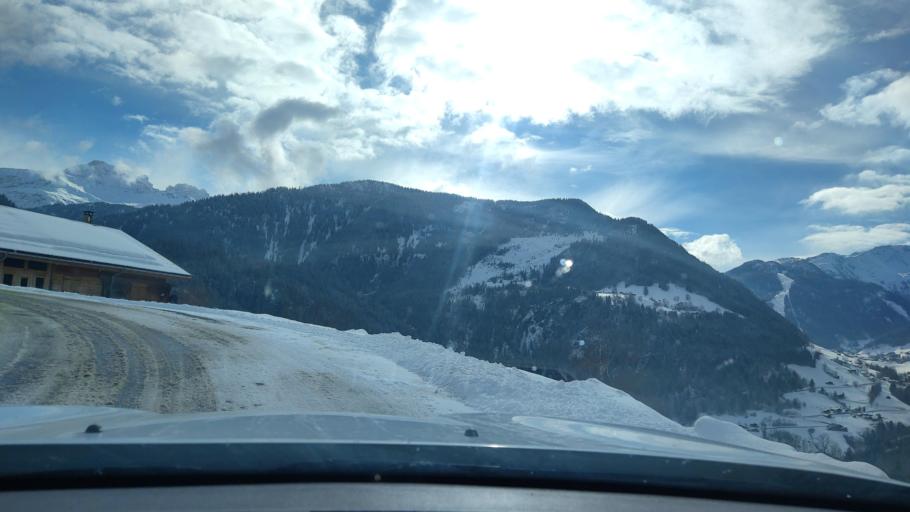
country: FR
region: Rhone-Alpes
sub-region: Departement de la Savoie
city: Beaufort
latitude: 45.7272
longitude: 6.5748
